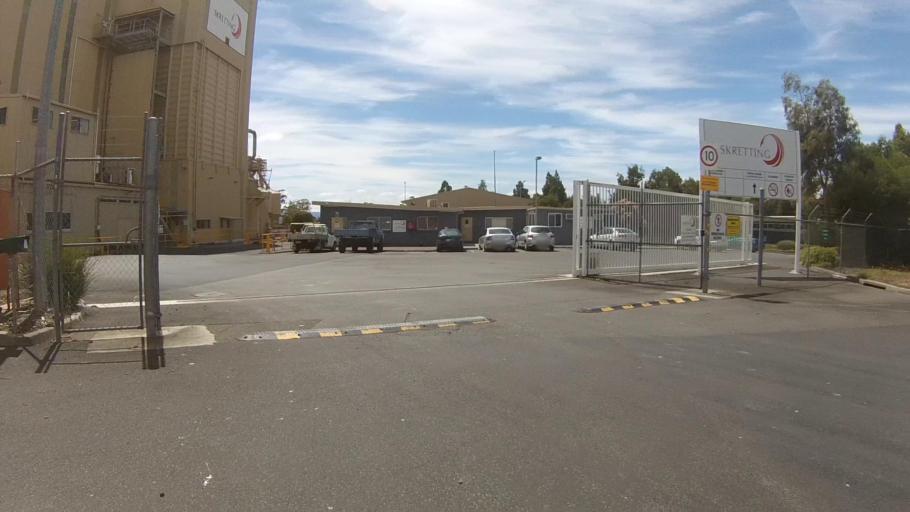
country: AU
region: Tasmania
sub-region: Clarence
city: Cambridge
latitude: -42.8324
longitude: 147.4504
